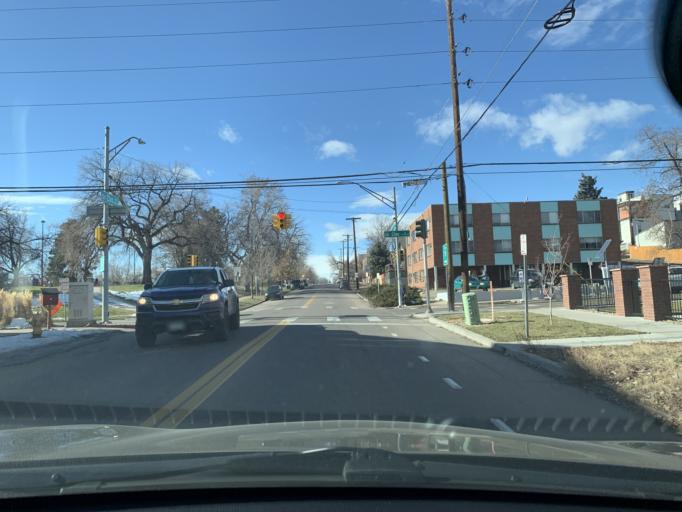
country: US
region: Colorado
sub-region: Denver County
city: Denver
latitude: 39.7513
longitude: -105.0202
